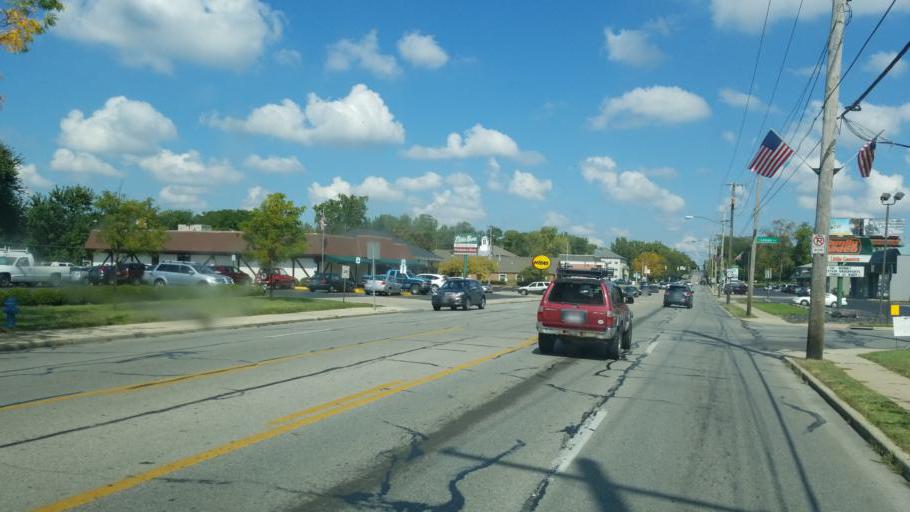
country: US
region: Ohio
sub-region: Franklin County
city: Worthington
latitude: 40.0752
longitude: -83.0188
